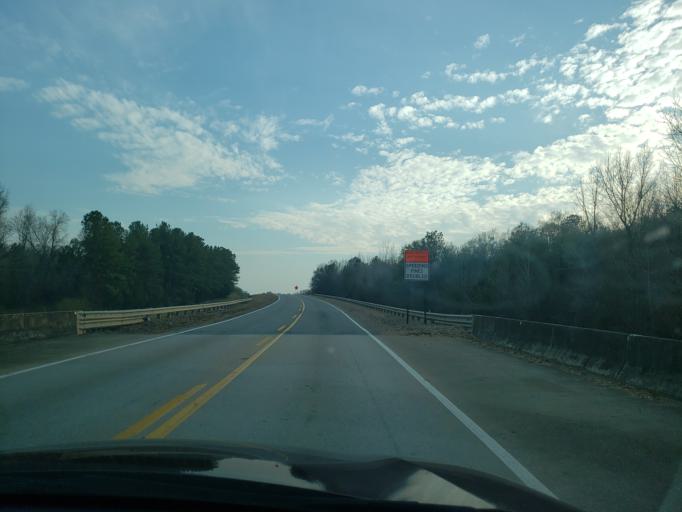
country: US
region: Alabama
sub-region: Hale County
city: Moundville
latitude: 32.9312
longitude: -87.6346
